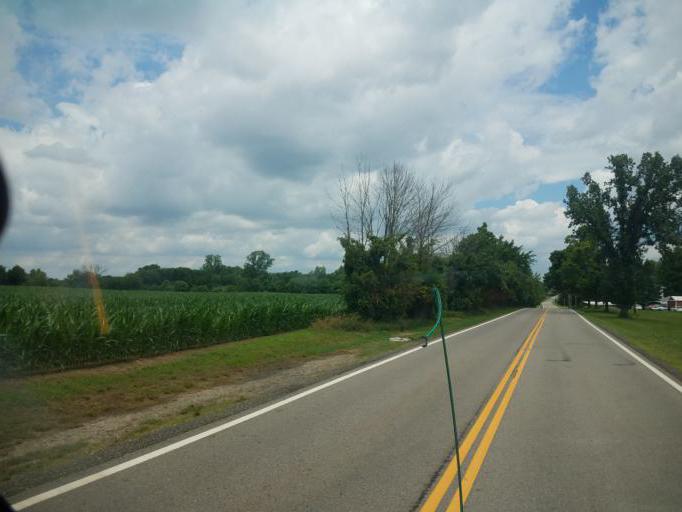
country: US
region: Ohio
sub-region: Huron County
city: Plymouth
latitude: 40.9808
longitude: -82.6710
